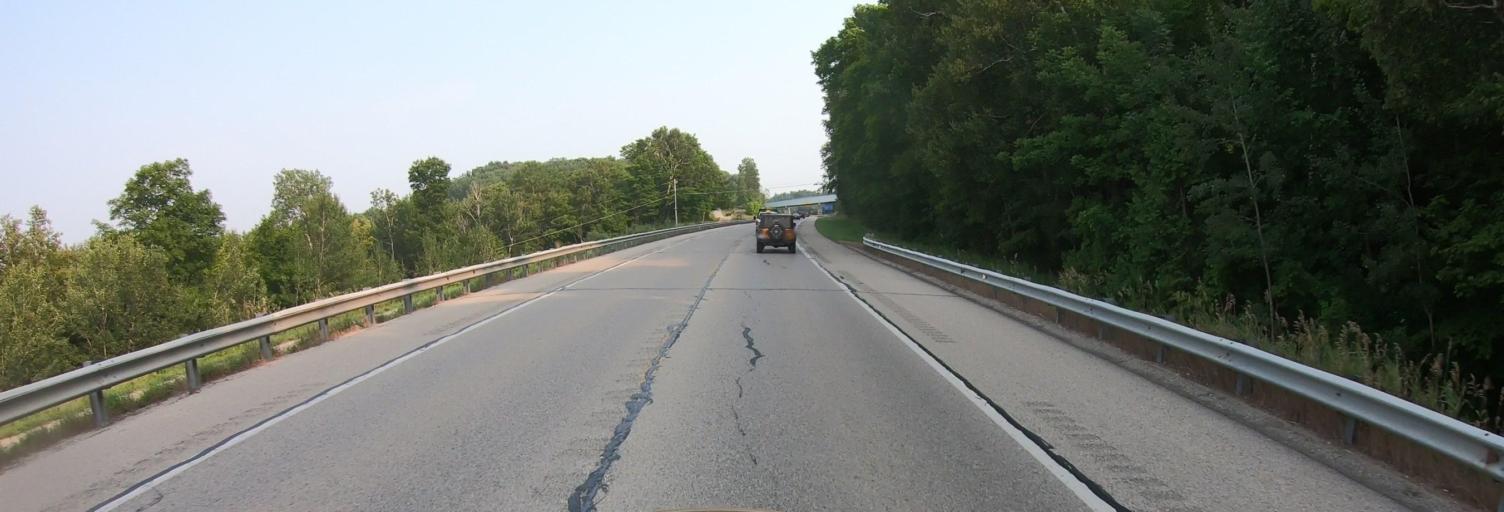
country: US
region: Michigan
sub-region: Charlevoix County
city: Charlevoix
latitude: 45.3654
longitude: -85.1216
